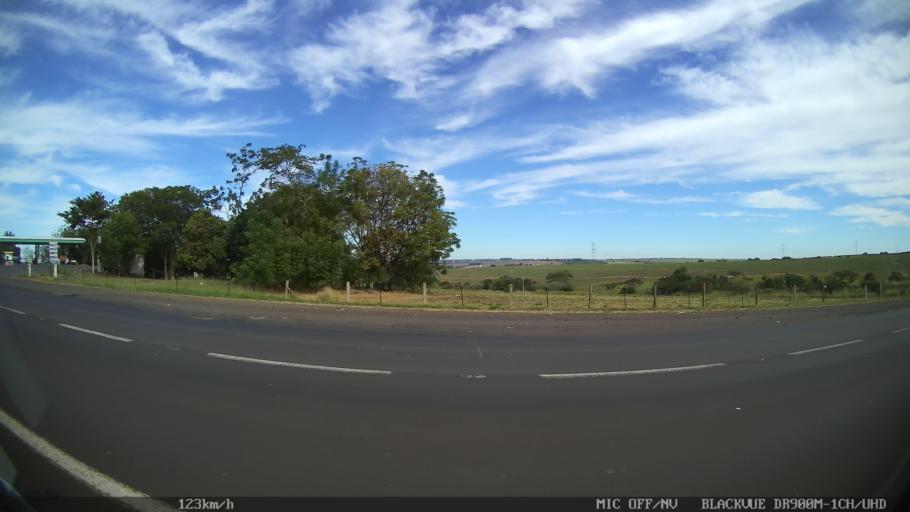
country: BR
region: Sao Paulo
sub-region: Taquaritinga
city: Taquaritinga
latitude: -21.5357
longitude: -48.5121
